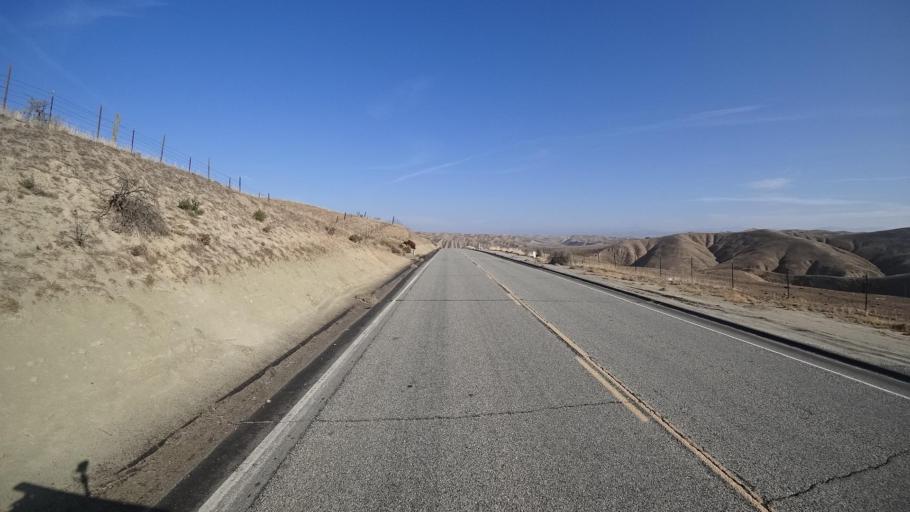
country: US
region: California
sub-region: Kern County
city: Oildale
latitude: 35.5174
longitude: -118.9801
